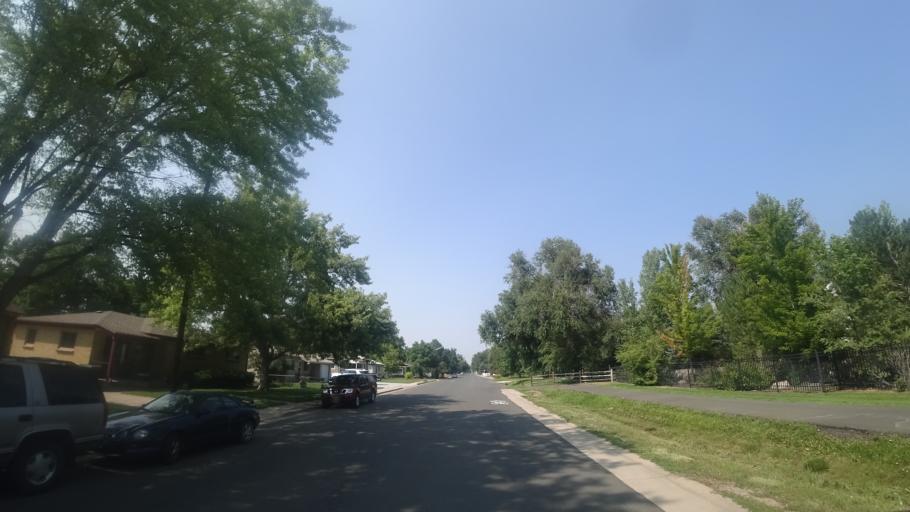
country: US
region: Colorado
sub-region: Arapahoe County
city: Englewood
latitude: 39.6303
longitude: -104.9785
